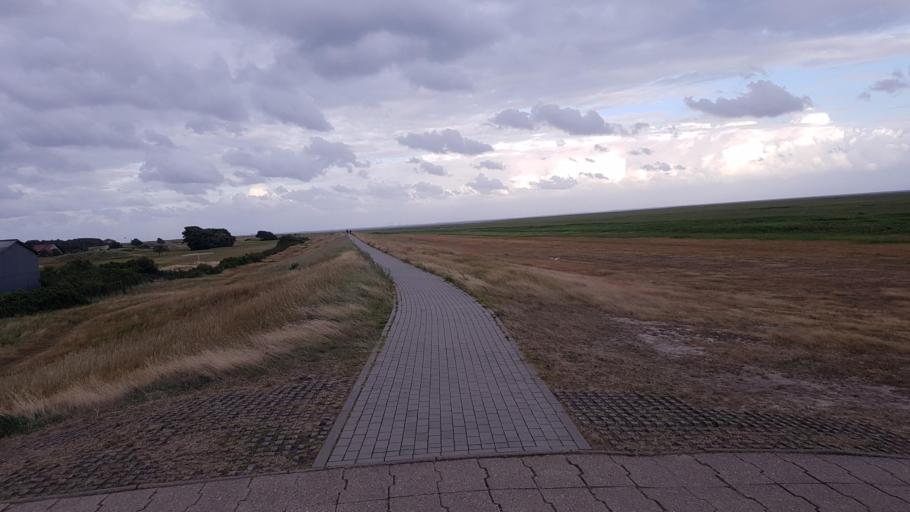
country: DE
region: Schleswig-Holstein
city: Sankt Peter-Ording
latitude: 54.2817
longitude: 8.6642
